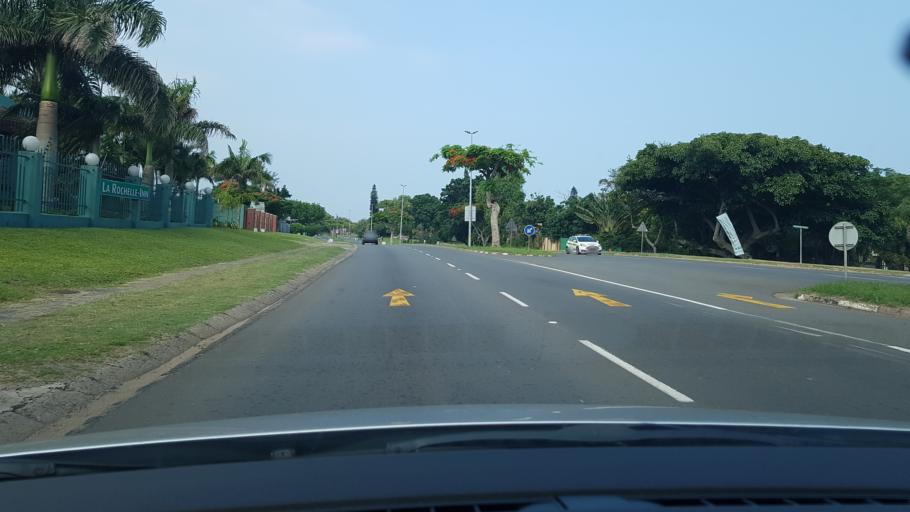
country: ZA
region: KwaZulu-Natal
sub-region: uThungulu District Municipality
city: Richards Bay
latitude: -28.7867
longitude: 32.0922
